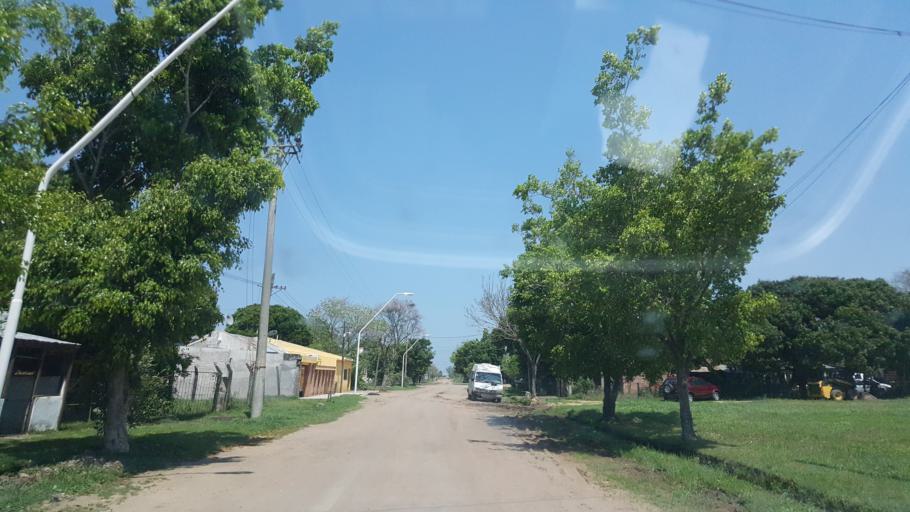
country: AR
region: Corrientes
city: Ita Ibate
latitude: -27.4275
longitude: -57.3369
